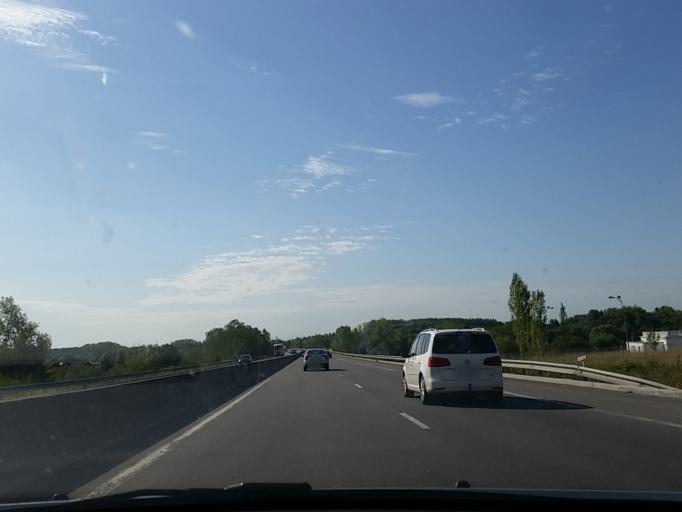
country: FR
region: Centre
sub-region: Departement du Cher
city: Vierzon
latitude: 47.2178
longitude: 2.1121
